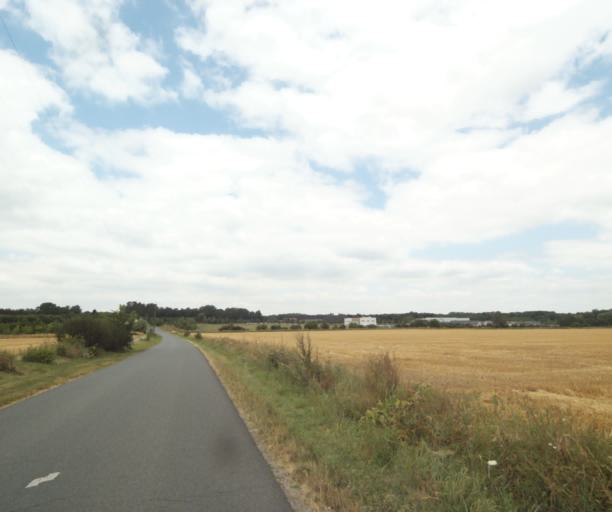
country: FR
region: Centre
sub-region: Departement du Loiret
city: Boigny-sur-Bionne
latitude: 47.9331
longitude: 2.0078
